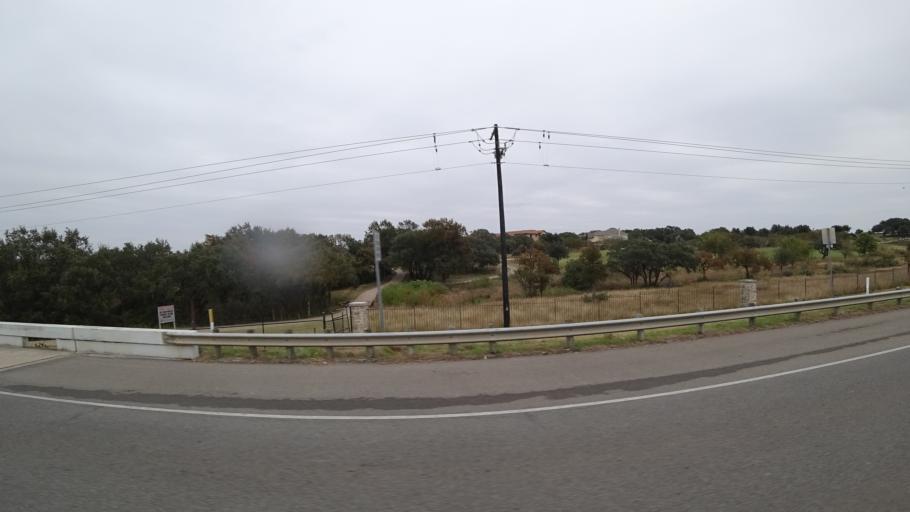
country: US
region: Texas
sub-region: Williamson County
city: Brushy Creek
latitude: 30.5027
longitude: -97.7768
